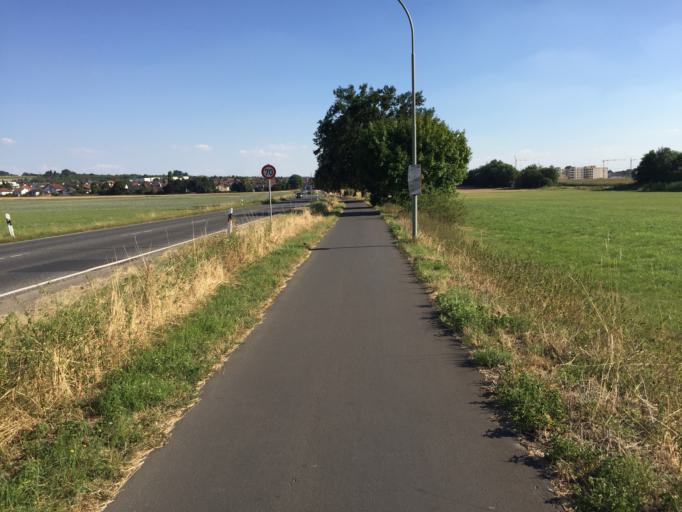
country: DE
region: Hesse
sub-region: Regierungsbezirk Giessen
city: Langgons
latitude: 50.5362
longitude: 8.6746
